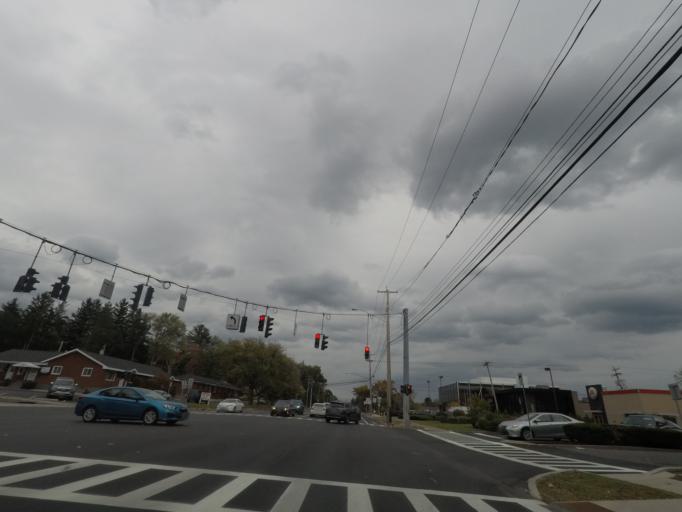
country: US
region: New York
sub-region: Albany County
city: McKownville
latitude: 42.6816
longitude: -73.8393
